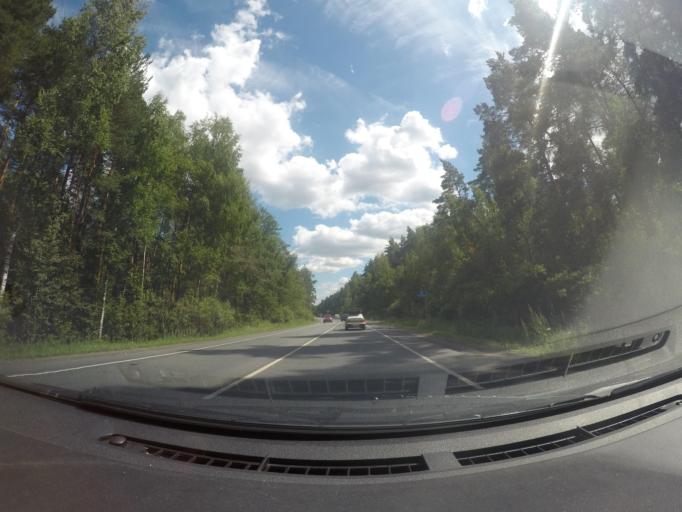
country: RU
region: Moskovskaya
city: Ramenskoye
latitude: 55.6366
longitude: 38.2573
